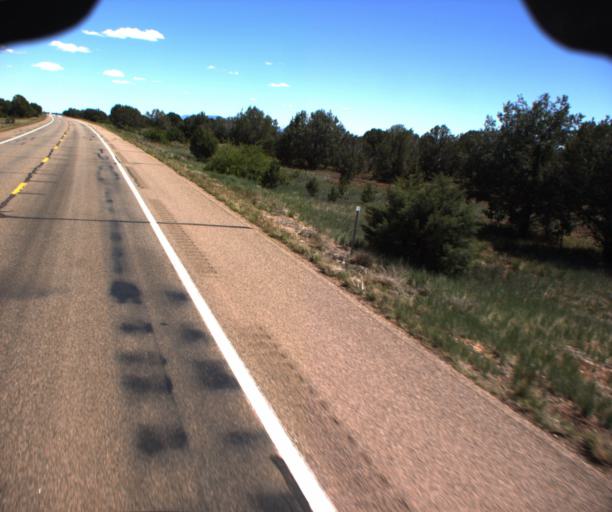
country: US
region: Arizona
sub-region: Yavapai County
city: Paulden
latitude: 35.0946
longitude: -112.4193
